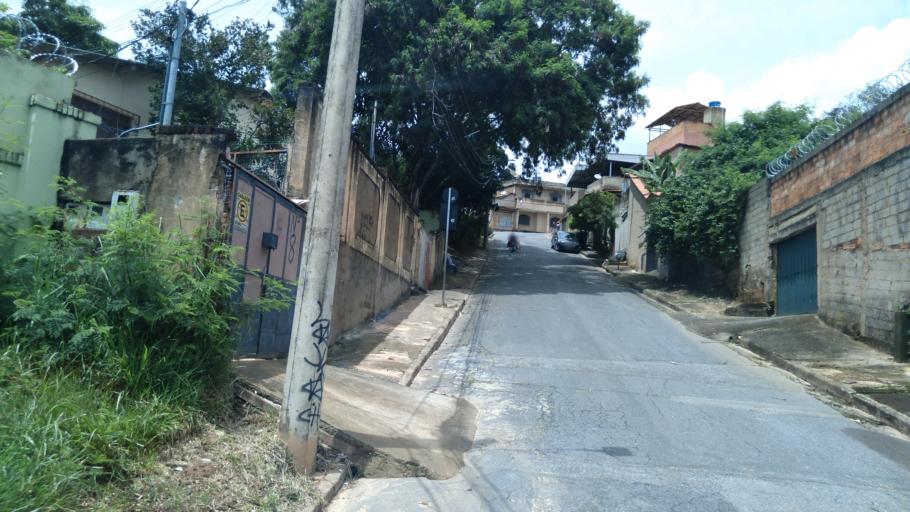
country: BR
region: Minas Gerais
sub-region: Belo Horizonte
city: Belo Horizonte
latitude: -19.9217
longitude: -43.9005
